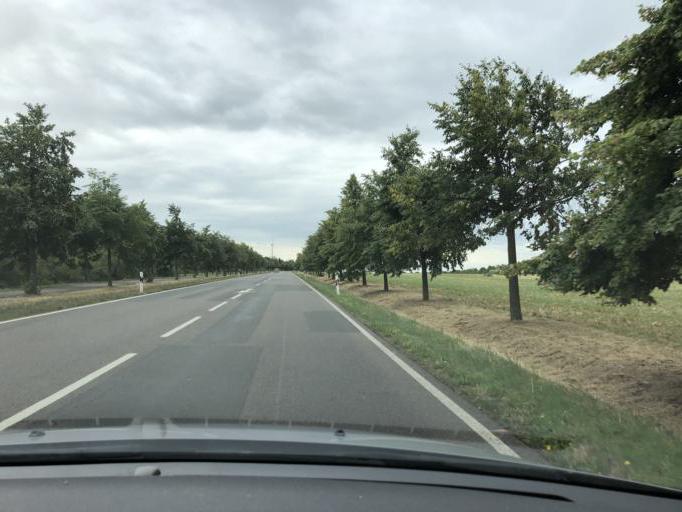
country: DE
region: Saxony
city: Rackwitz
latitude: 51.4193
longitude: 12.4027
